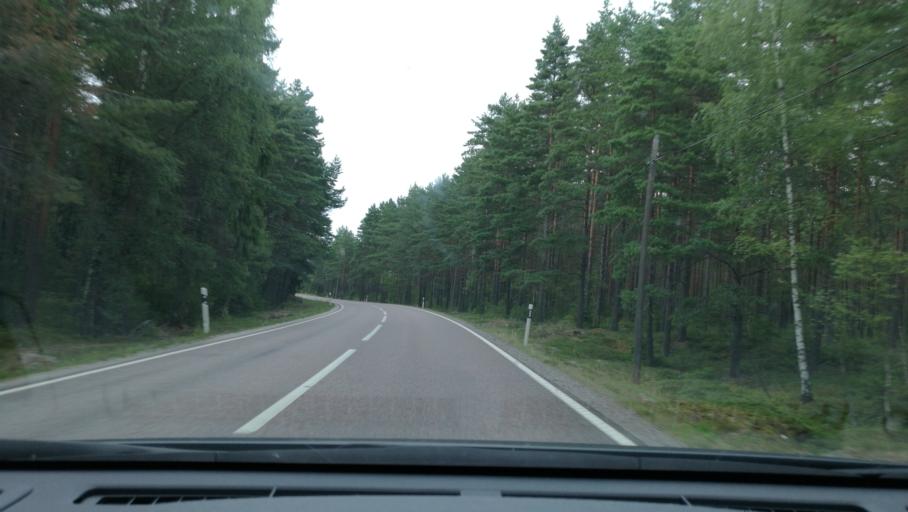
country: SE
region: Vaestmanland
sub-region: Kungsors Kommun
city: Kungsoer
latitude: 59.3044
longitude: 16.1077
